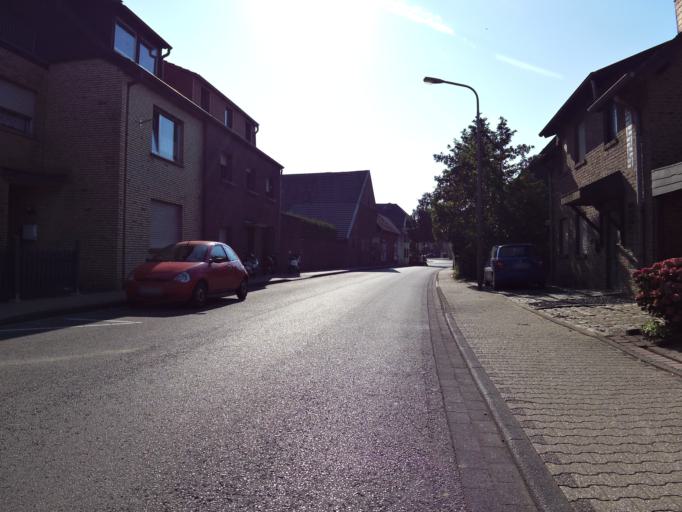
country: DE
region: North Rhine-Westphalia
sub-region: Regierungsbezirk Koln
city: Alsdorf
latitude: 50.8406
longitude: 6.1843
